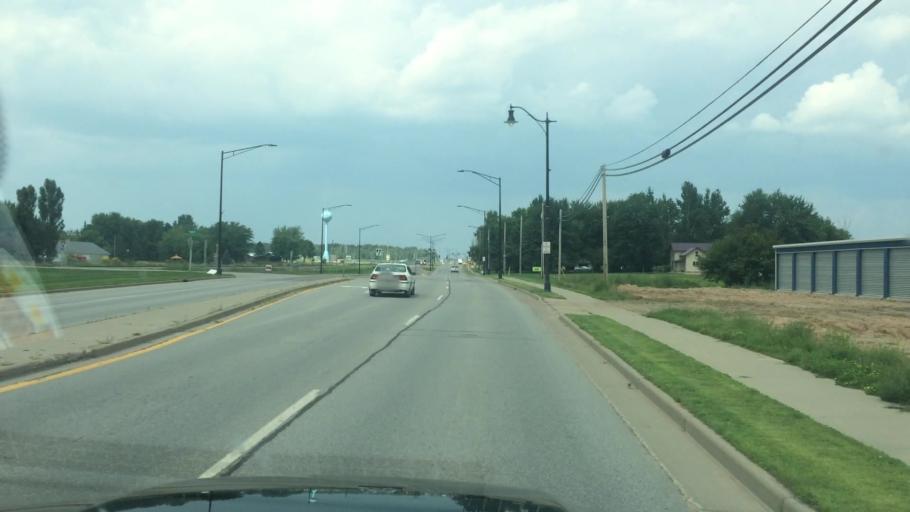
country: US
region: Wisconsin
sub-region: Clark County
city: Colby
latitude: 44.9124
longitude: -90.3154
